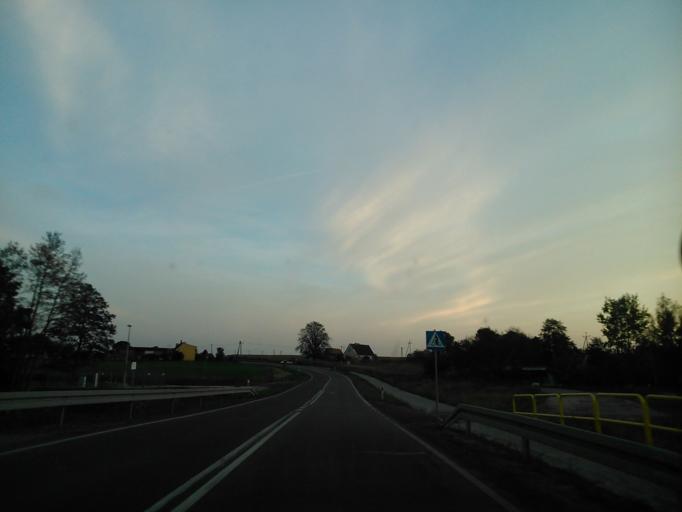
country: PL
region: Kujawsko-Pomorskie
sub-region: Powiat wabrzeski
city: Debowa Laka
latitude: 53.2008
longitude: 19.0371
